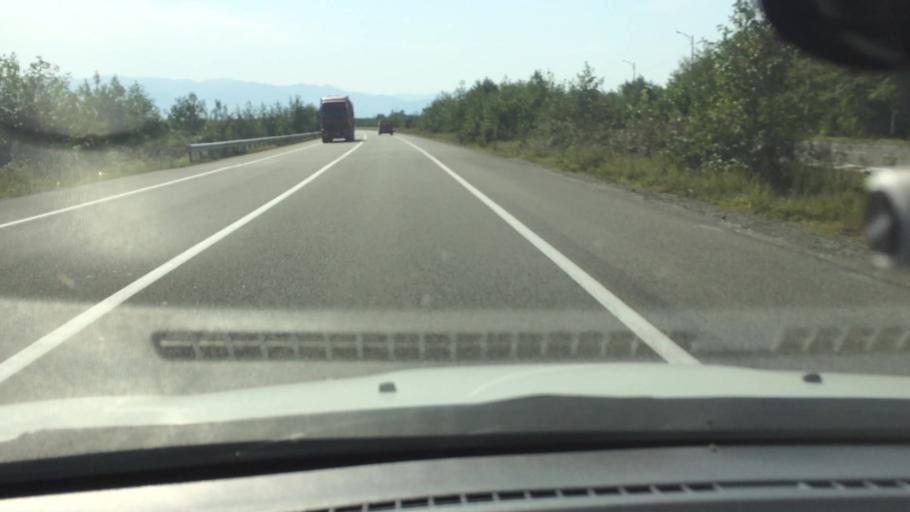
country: GE
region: Guria
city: Urek'i
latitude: 41.9229
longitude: 41.7739
